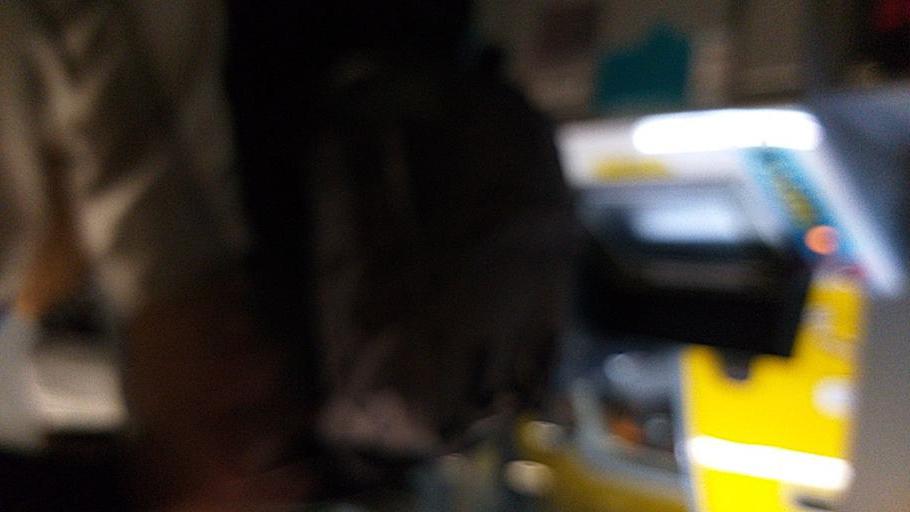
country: SG
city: Singapore
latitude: 1.3555
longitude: 103.9914
